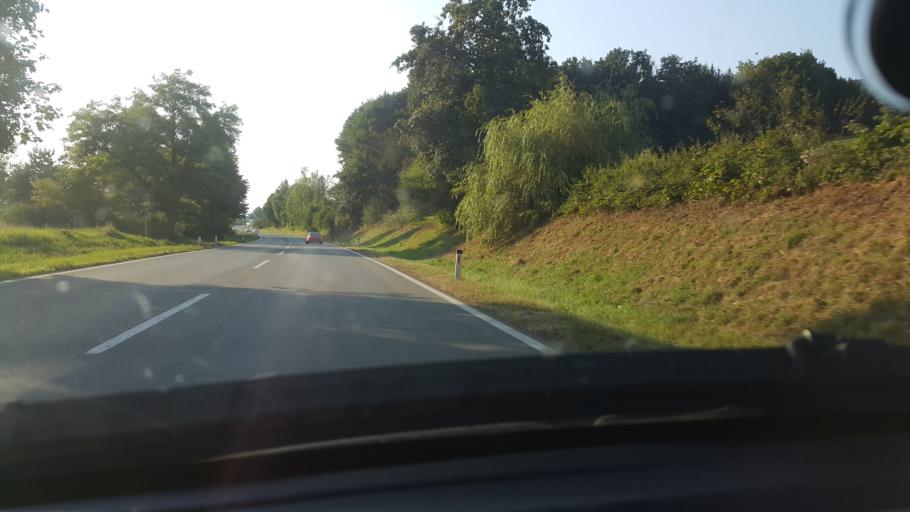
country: AT
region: Carinthia
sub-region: Politischer Bezirk Klagenfurt Land
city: Moosburg
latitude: 46.6654
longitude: 14.1687
